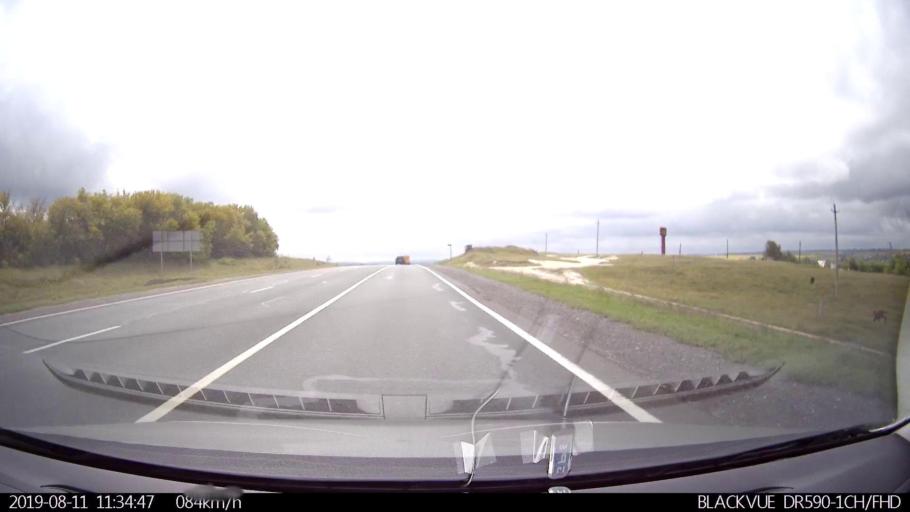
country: RU
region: Ulyanovsk
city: Silikatnyy
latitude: 54.0135
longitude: 48.2174
